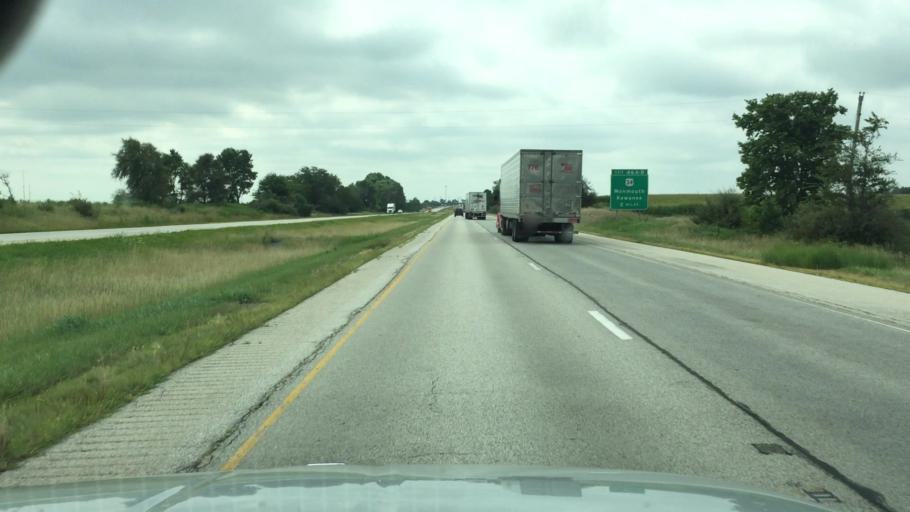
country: US
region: Illinois
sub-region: Knox County
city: Galesburg
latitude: 41.0167
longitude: -90.3349
